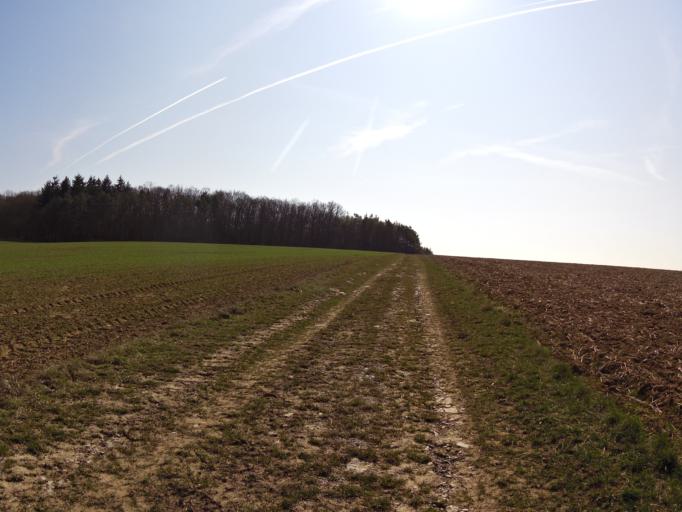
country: DE
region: Bavaria
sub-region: Regierungsbezirk Unterfranken
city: Estenfeld
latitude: 49.8098
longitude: 10.0116
